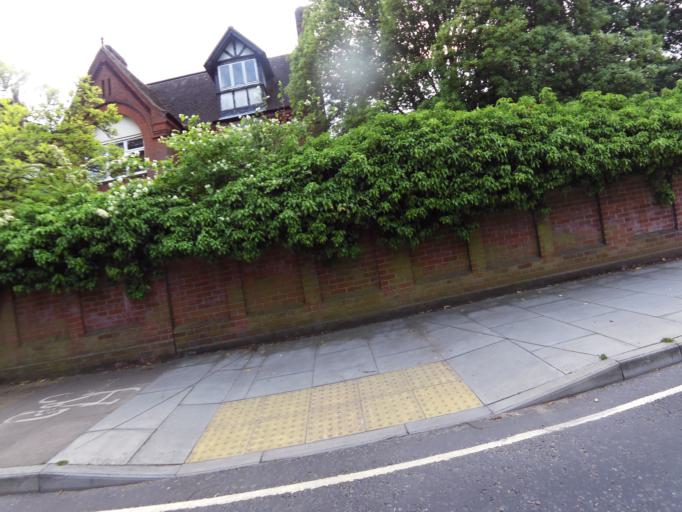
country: GB
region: England
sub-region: Suffolk
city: Ipswich
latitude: 52.0688
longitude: 1.1535
